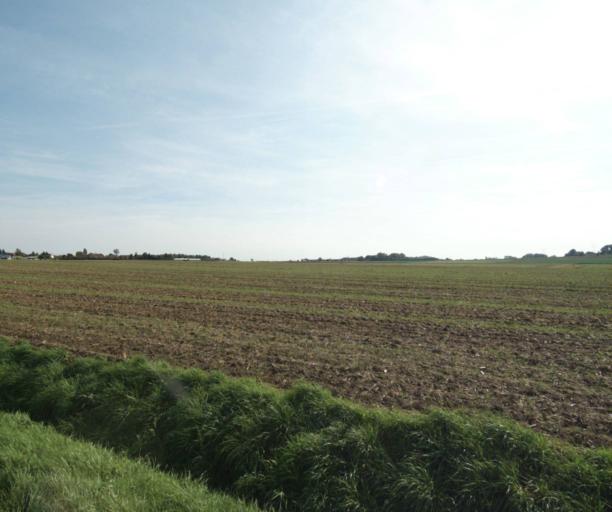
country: FR
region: Nord-Pas-de-Calais
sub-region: Departement du Nord
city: Ennetieres-en-Weppes
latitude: 50.6419
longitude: 2.9501
